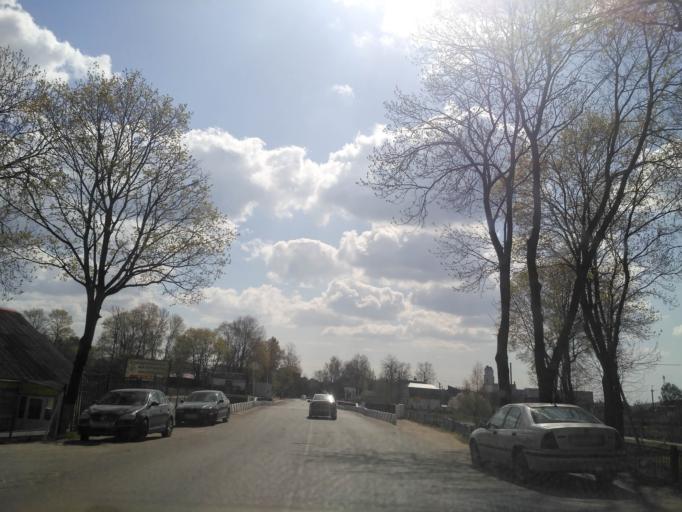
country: BY
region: Minsk
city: Radashkovichy
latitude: 54.1598
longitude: 27.2362
